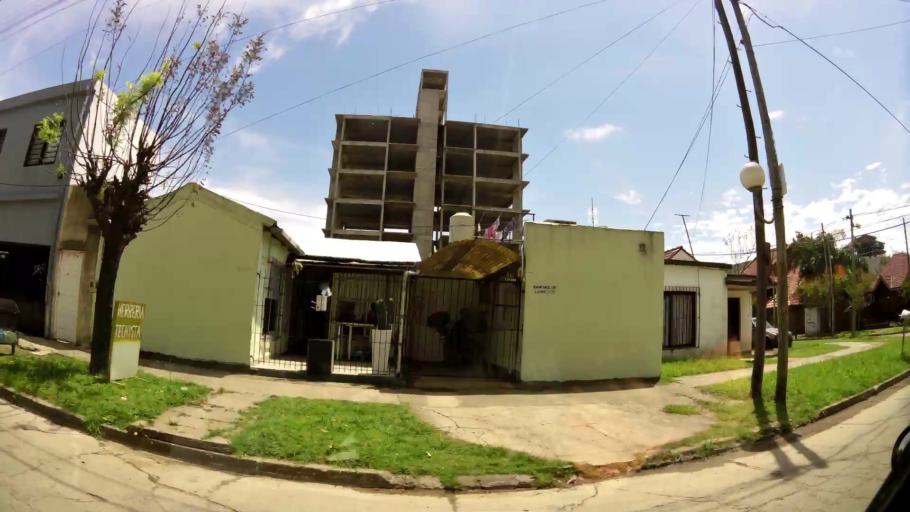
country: AR
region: Buenos Aires
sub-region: Partido de Quilmes
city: Quilmes
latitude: -34.7842
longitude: -58.2665
